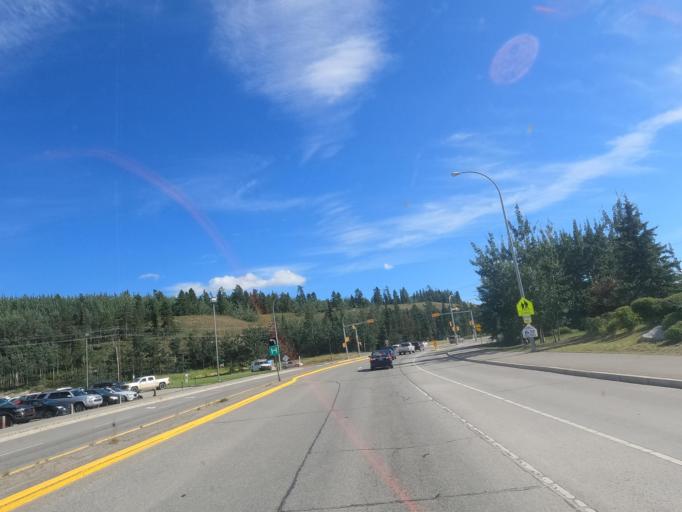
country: CA
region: Yukon
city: Whitehorse
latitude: 60.7135
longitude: -135.0423
